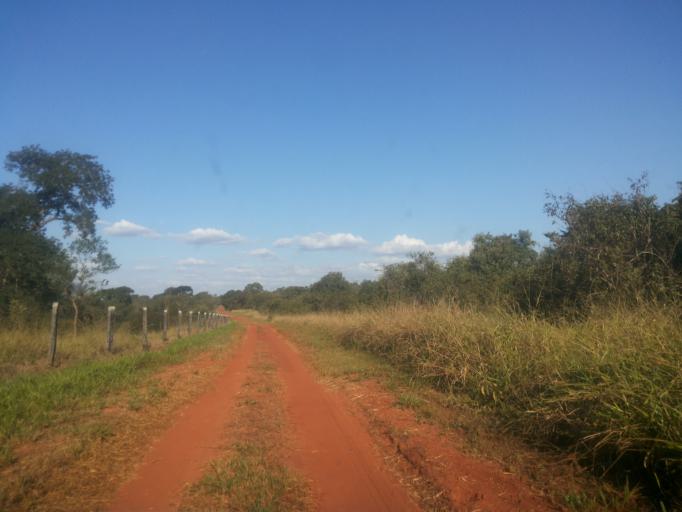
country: BR
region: Minas Gerais
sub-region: Santa Vitoria
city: Santa Vitoria
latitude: -19.0152
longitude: -50.4490
